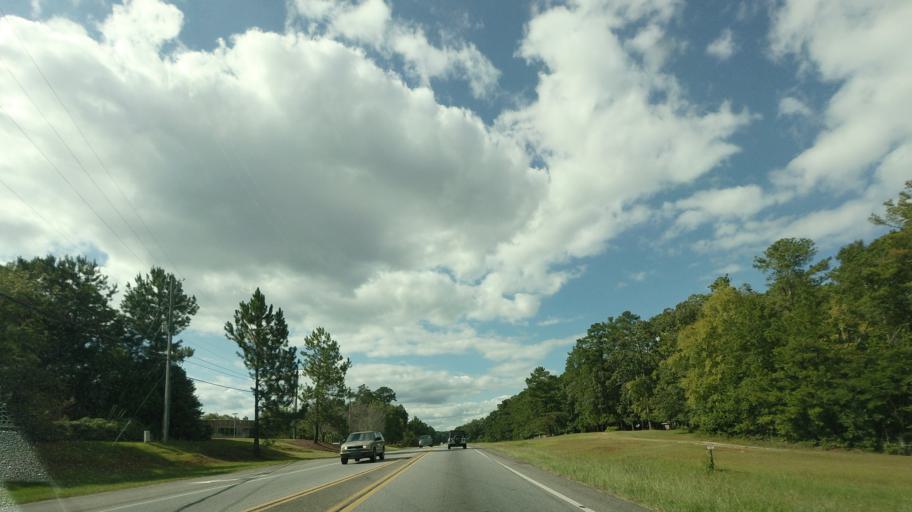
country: US
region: Georgia
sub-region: Bibb County
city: Macon
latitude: 32.9381
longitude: -83.7182
